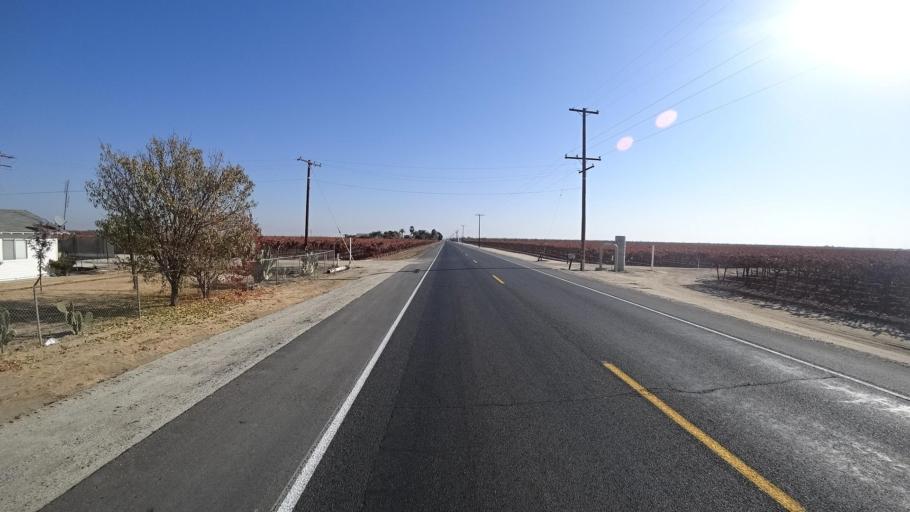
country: US
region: California
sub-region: Kern County
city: McFarland
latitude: 35.7178
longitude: -119.2633
